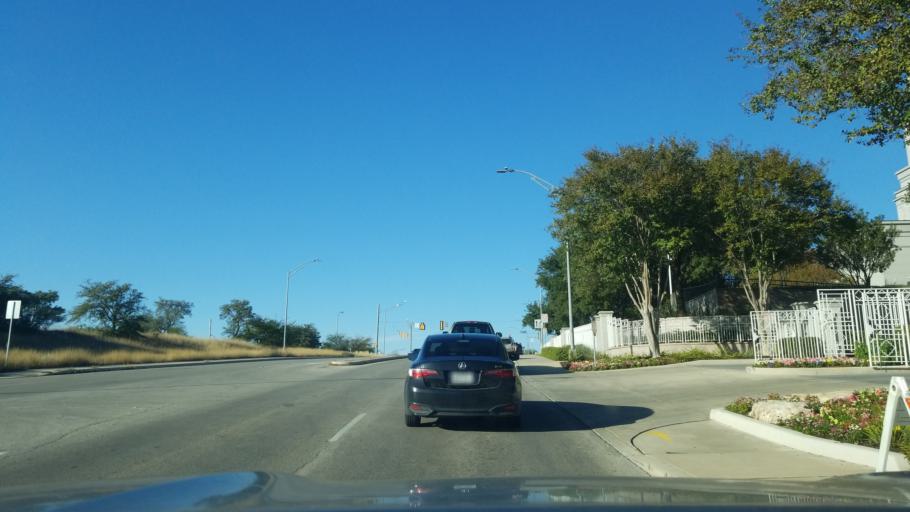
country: US
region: Texas
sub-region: Bexar County
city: Hollywood Park
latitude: 29.6408
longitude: -98.4891
